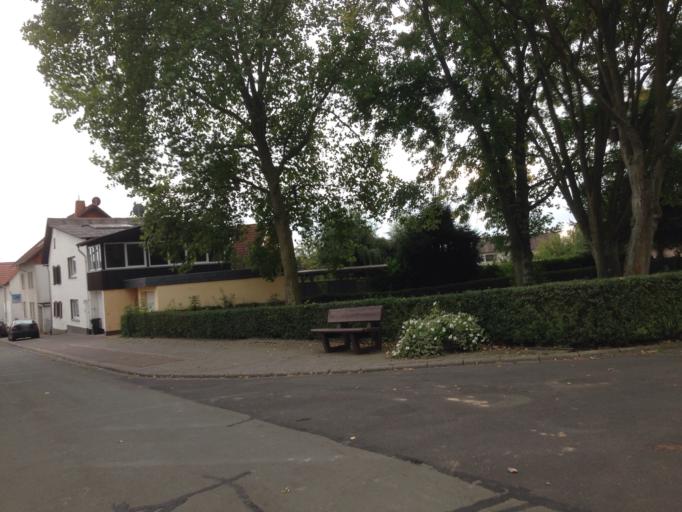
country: DE
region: Hesse
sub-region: Regierungsbezirk Giessen
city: Alten Buseck
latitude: 50.6239
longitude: 8.7527
